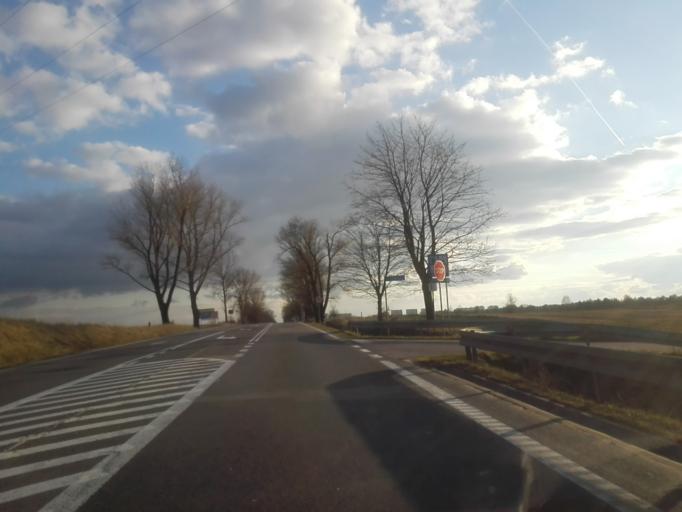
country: PL
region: Podlasie
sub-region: Suwalki
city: Suwalki
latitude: 54.1368
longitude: 22.9565
